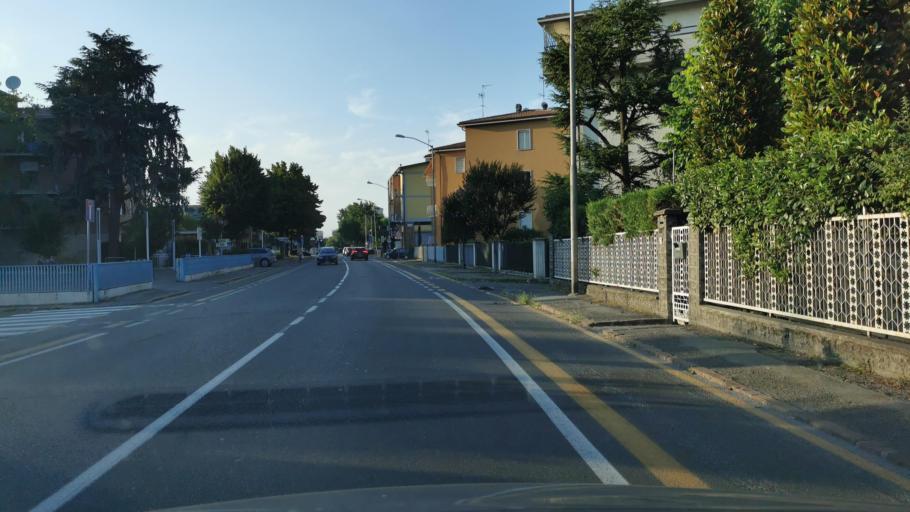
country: IT
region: Emilia-Romagna
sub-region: Provincia di Modena
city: Modena
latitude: 44.6257
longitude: 10.9272
